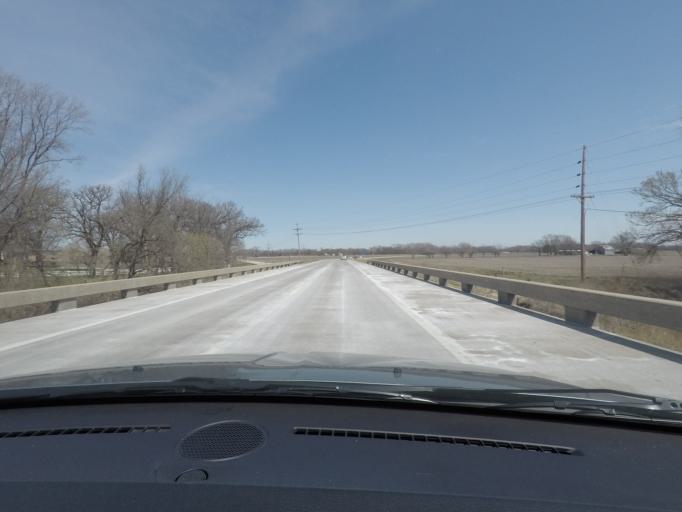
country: US
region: Kansas
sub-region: Lyon County
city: Emporia
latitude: 38.4277
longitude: -96.1802
